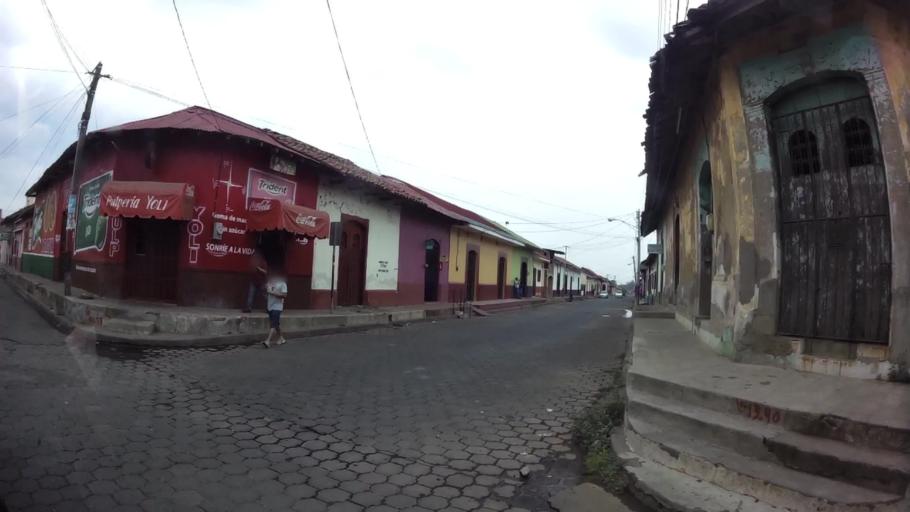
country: NI
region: Leon
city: Leon
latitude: 12.4332
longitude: -86.8831
